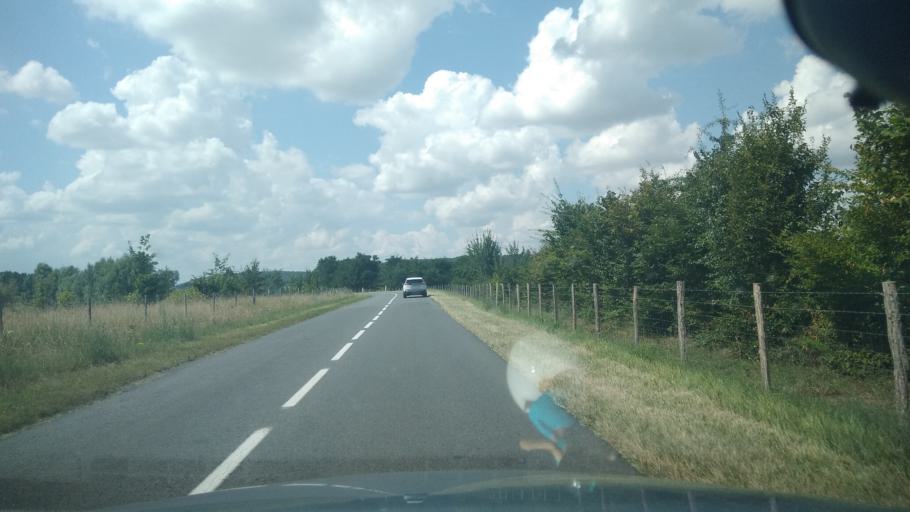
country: FR
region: Poitou-Charentes
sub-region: Departement de la Vienne
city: Dange-Saint-Romain
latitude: 46.9193
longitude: 0.5803
